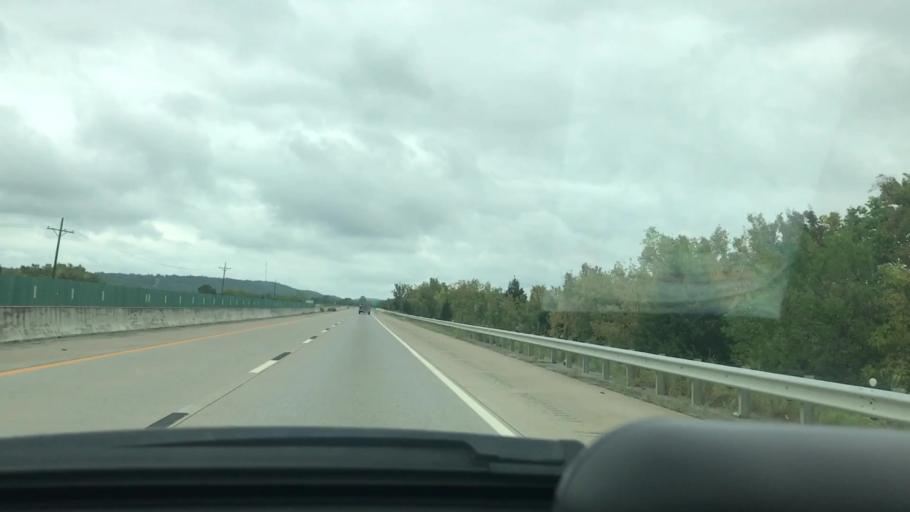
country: US
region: Oklahoma
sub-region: Pittsburg County
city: Krebs
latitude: 35.0418
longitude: -95.7111
